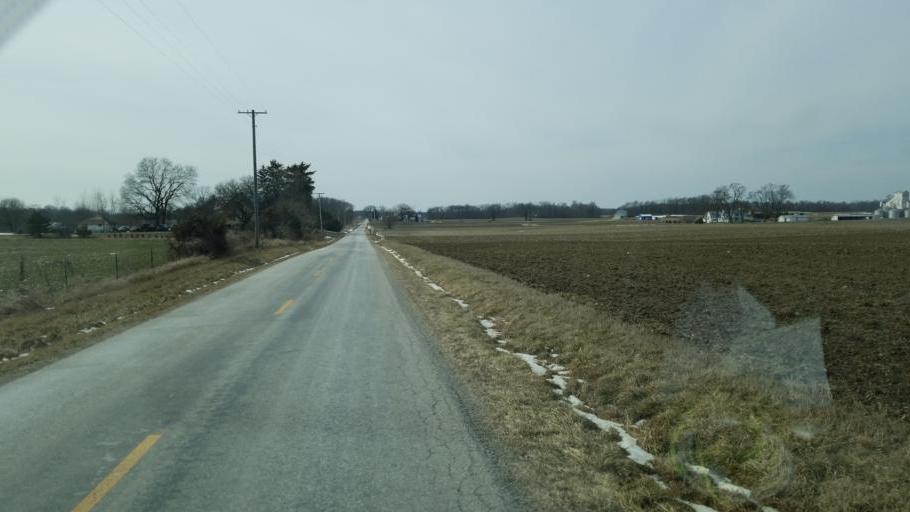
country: US
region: Ohio
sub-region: Marion County
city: Prospect
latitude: 40.3647
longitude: -83.1569
